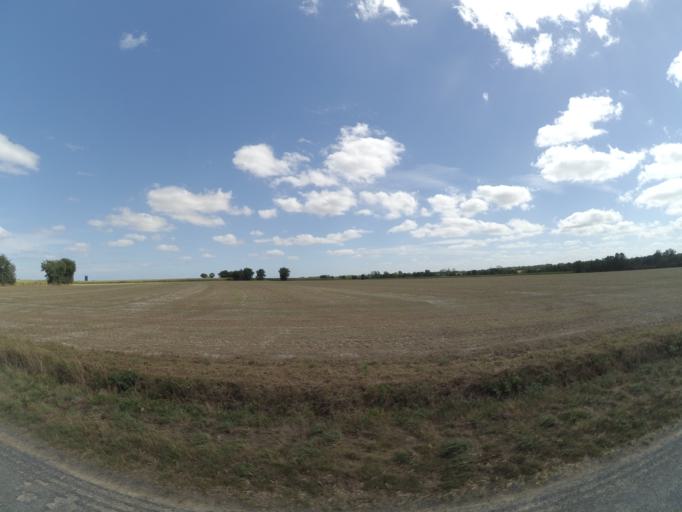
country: FR
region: Pays de la Loire
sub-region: Departement de la Loire-Atlantique
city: Saint-Hilaire-de-Clisson
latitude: 47.0491
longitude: -1.3371
